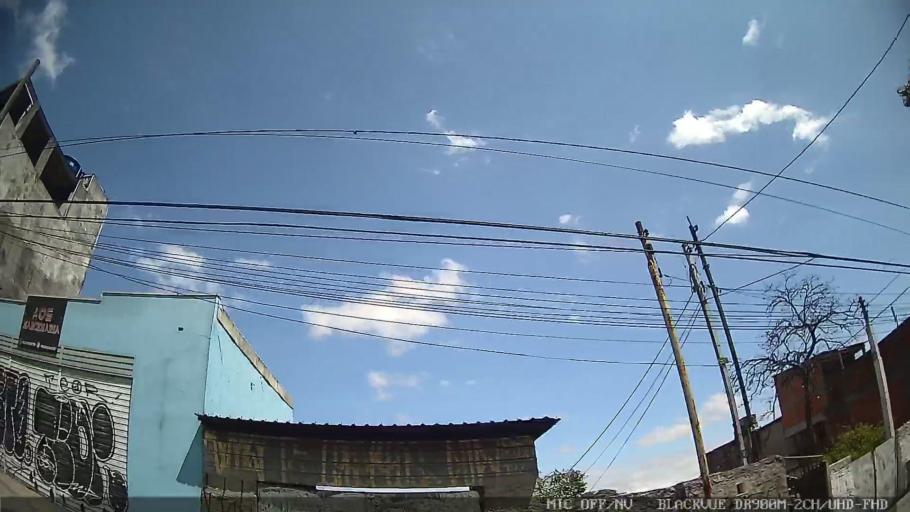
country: BR
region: Sao Paulo
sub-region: Guarulhos
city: Guarulhos
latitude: -23.5385
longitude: -46.4795
